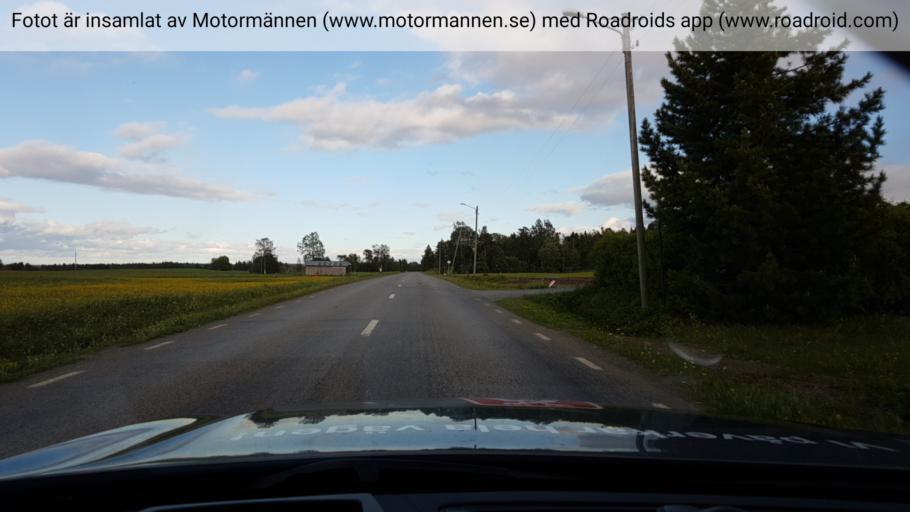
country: SE
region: Jaemtland
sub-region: Krokoms Kommun
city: Krokom
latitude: 63.1462
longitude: 14.1733
